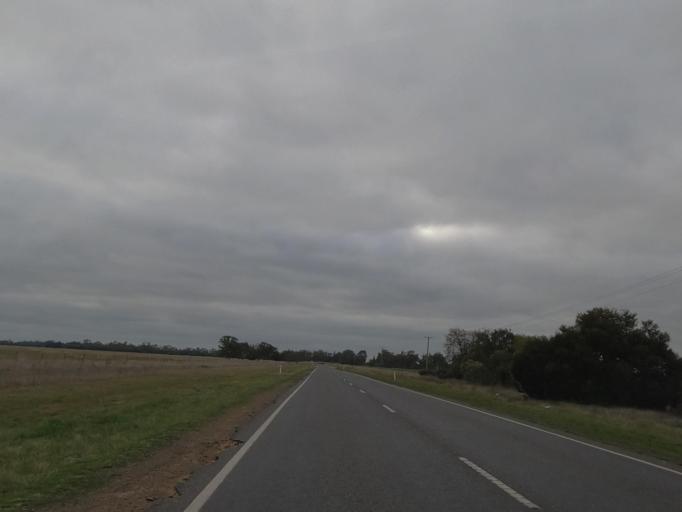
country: AU
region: Victoria
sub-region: Greater Bendigo
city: Long Gully
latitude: -36.4545
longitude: 143.9655
